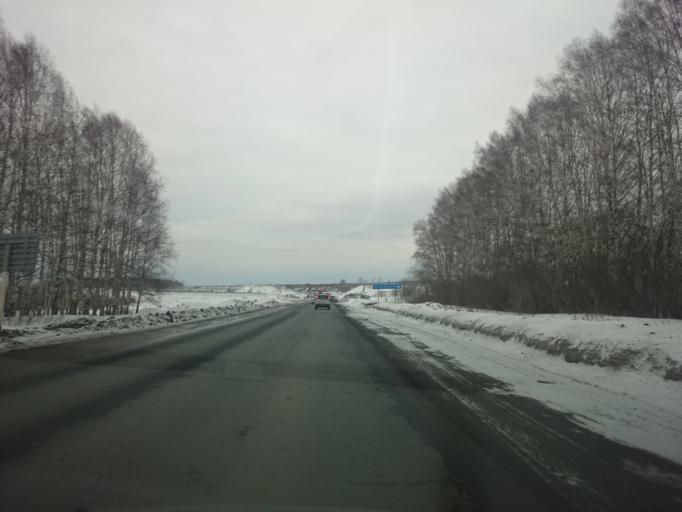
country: RU
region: Sverdlovsk
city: Achit
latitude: 56.7858
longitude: 57.8776
